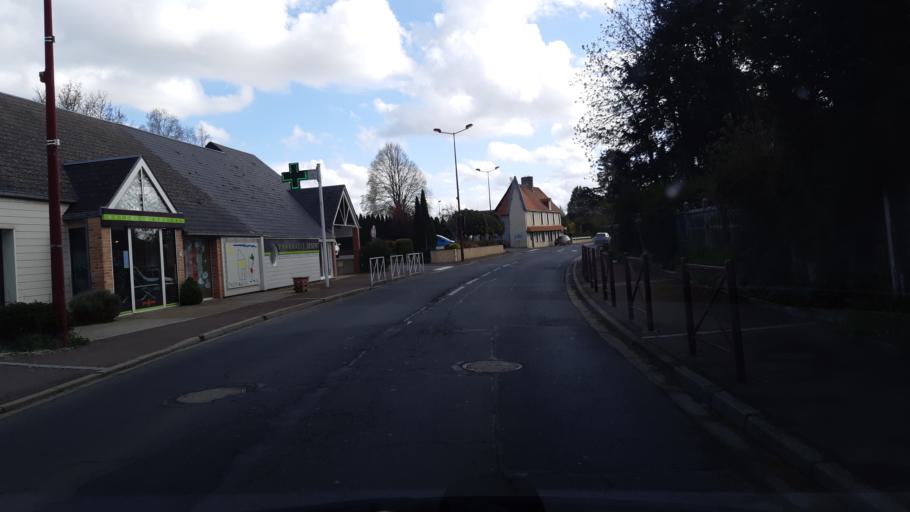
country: FR
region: Lower Normandy
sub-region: Departement de la Manche
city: Agneaux
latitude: 49.0463
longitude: -1.1280
